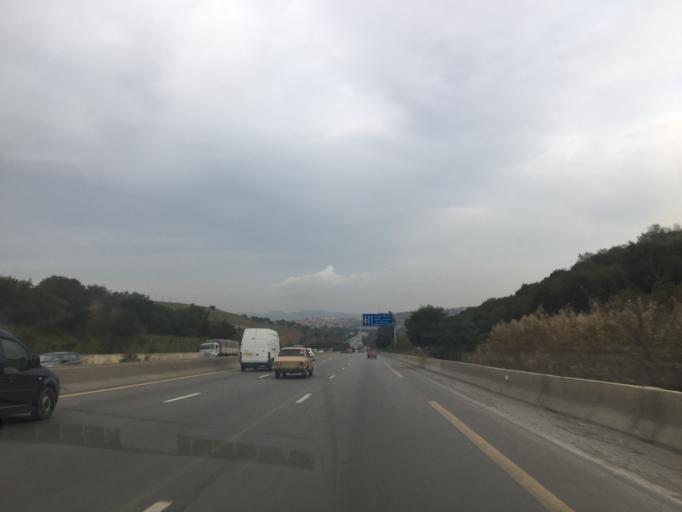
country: DZ
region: Bouira
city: Bouira
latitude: 36.3383
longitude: 3.9264
